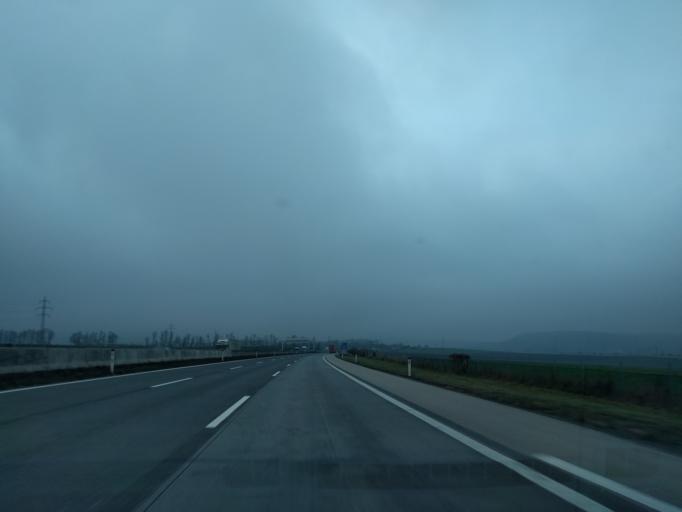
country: AT
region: Lower Austria
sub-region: Politischer Bezirk Melk
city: Loosdorf
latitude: 48.1898
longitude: 15.4019
